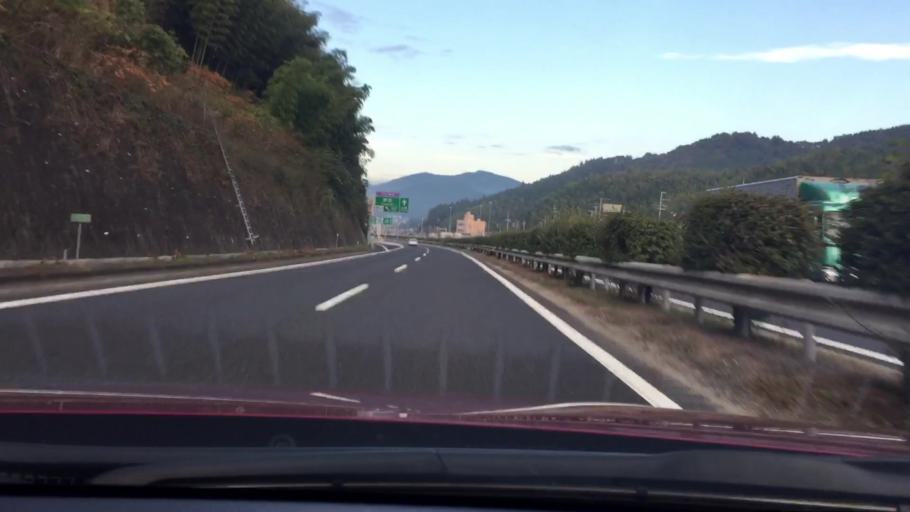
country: JP
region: Hyogo
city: Himeji
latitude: 34.9619
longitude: 134.6963
